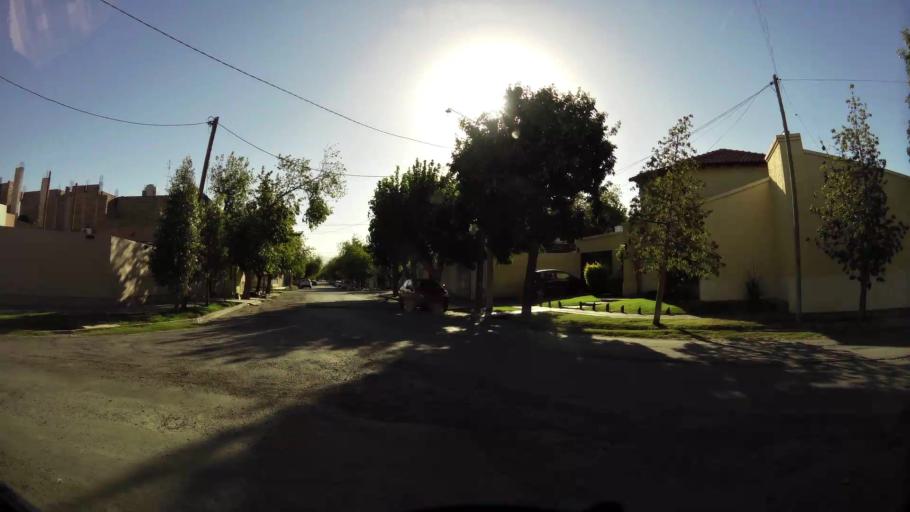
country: AR
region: San Juan
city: Villa Krause
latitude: -31.5612
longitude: -68.5175
